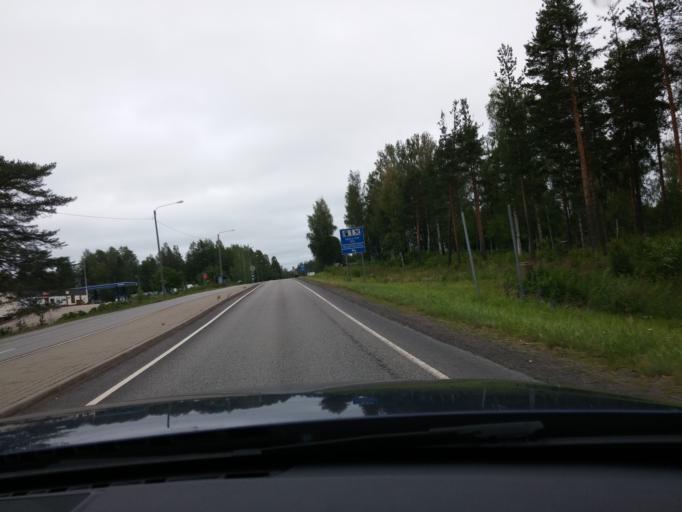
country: FI
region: Central Finland
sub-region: Saarijaervi-Viitasaari
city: Saarijaervi
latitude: 62.6983
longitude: 25.2845
